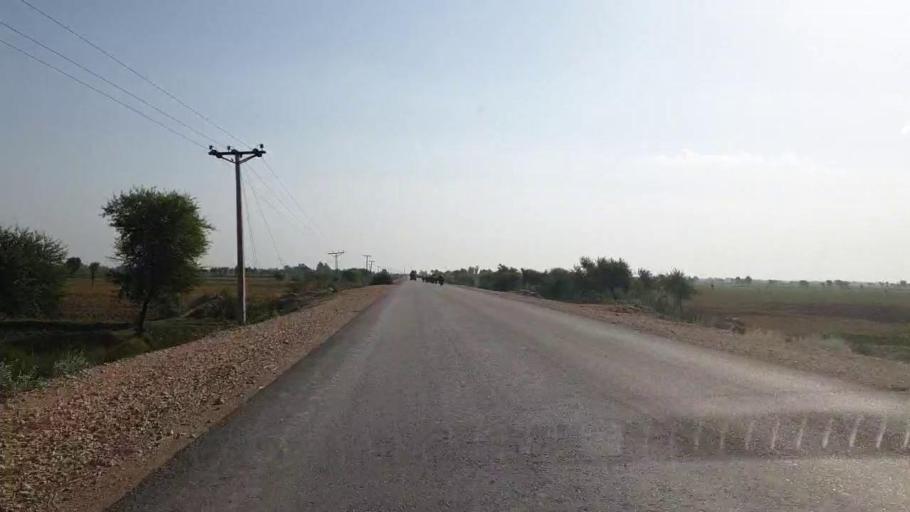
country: PK
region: Sindh
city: Tando Bago
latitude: 24.6573
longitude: 69.0006
